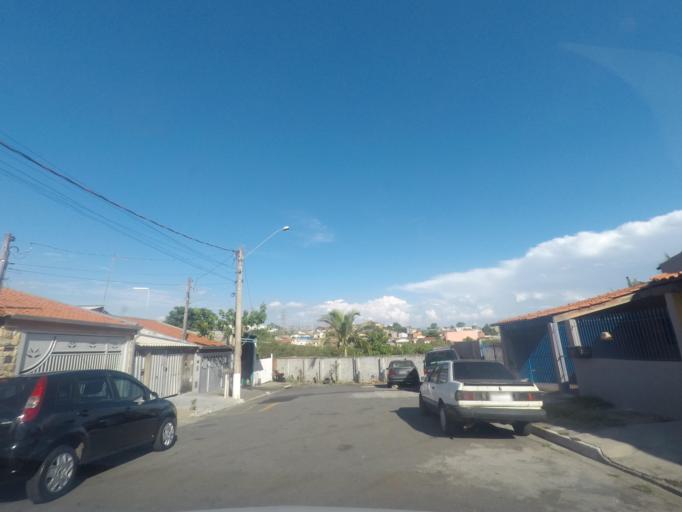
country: BR
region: Sao Paulo
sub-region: Sumare
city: Sumare
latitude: -22.8116
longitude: -47.2636
